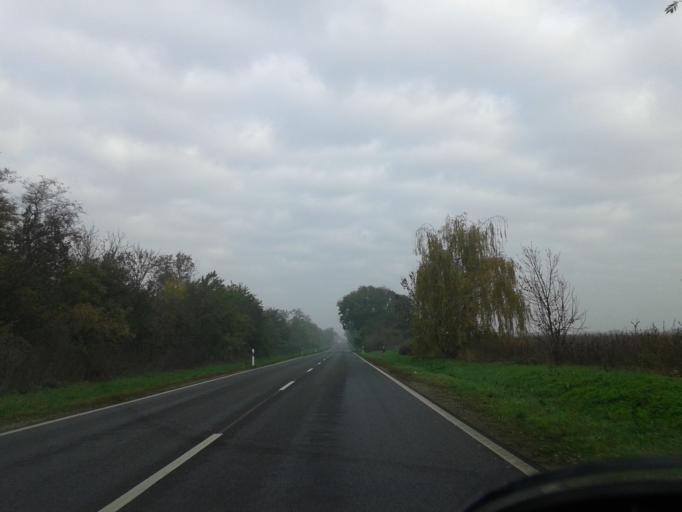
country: HU
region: Pest
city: Szazhalombatta
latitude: 47.3428
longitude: 18.8996
